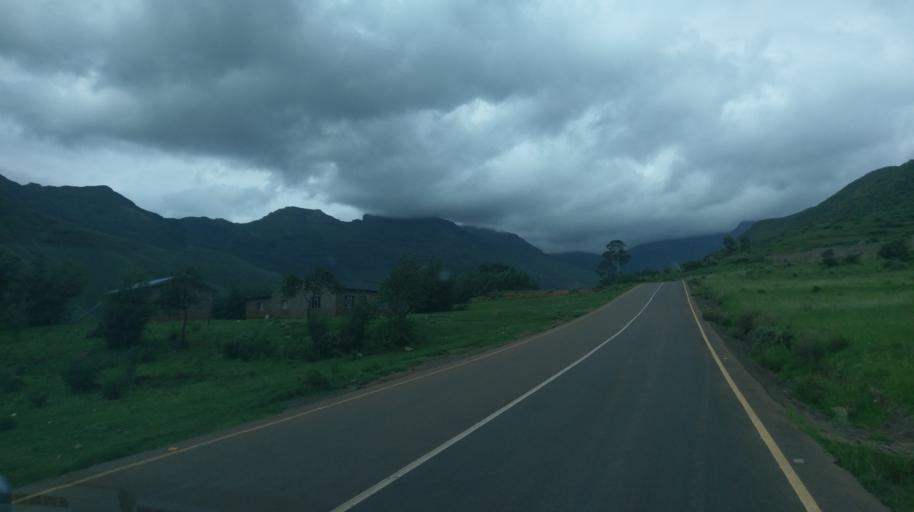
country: LS
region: Butha-Buthe
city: Butha-Buthe
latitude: -29.0501
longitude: 28.3302
